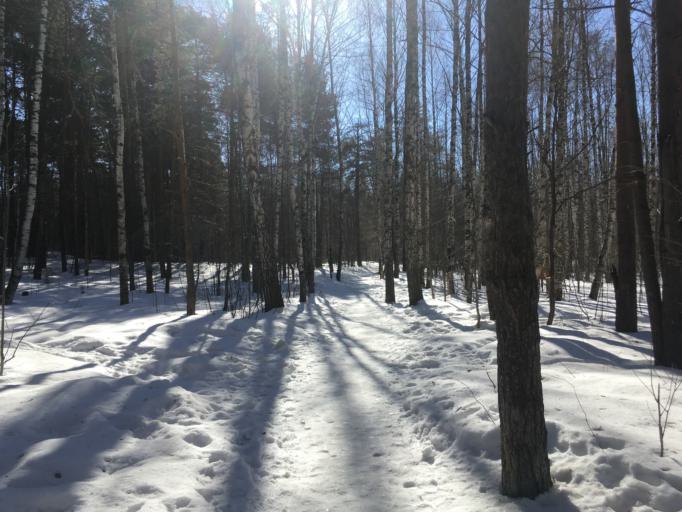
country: RU
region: Perm
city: Kondratovo
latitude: 57.9925
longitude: 56.1637
